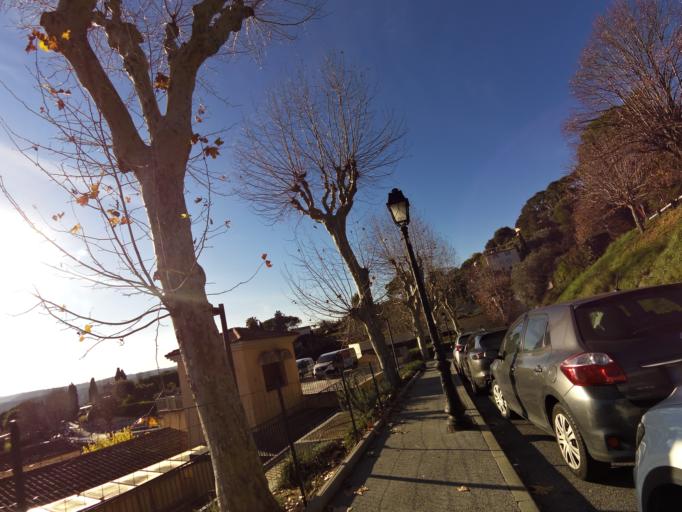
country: FR
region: Provence-Alpes-Cote d'Azur
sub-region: Departement des Alpes-Maritimes
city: Saint-Paul-de-Vence
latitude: 43.6989
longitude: 7.1195
